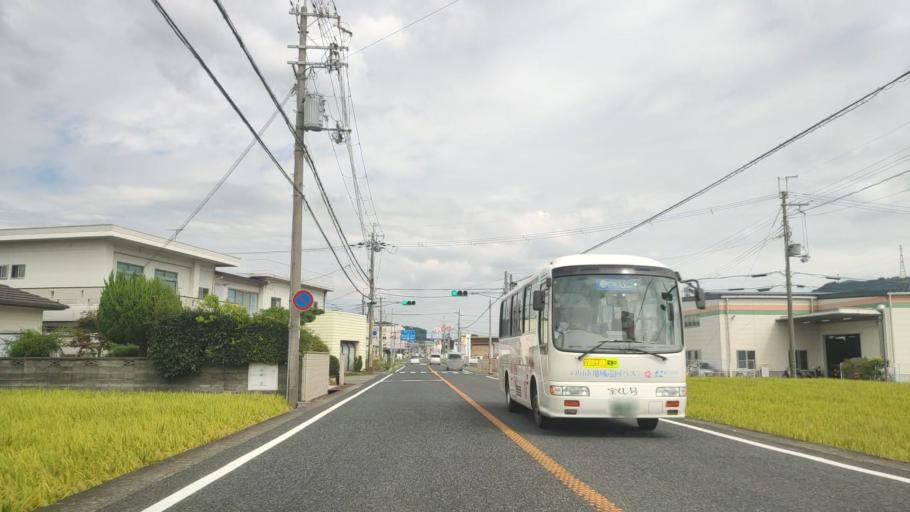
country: JP
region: Wakayama
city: Iwade
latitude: 34.2737
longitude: 135.4377
